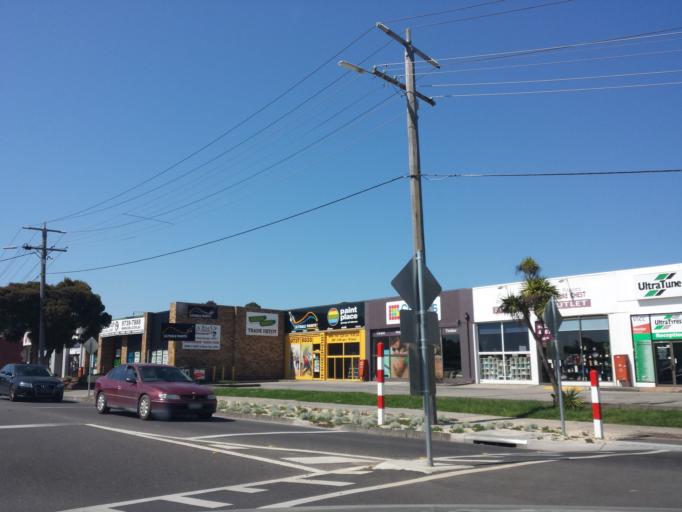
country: AU
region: Victoria
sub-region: Yarra Ranges
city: Lilydale
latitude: -37.7578
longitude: 145.3456
